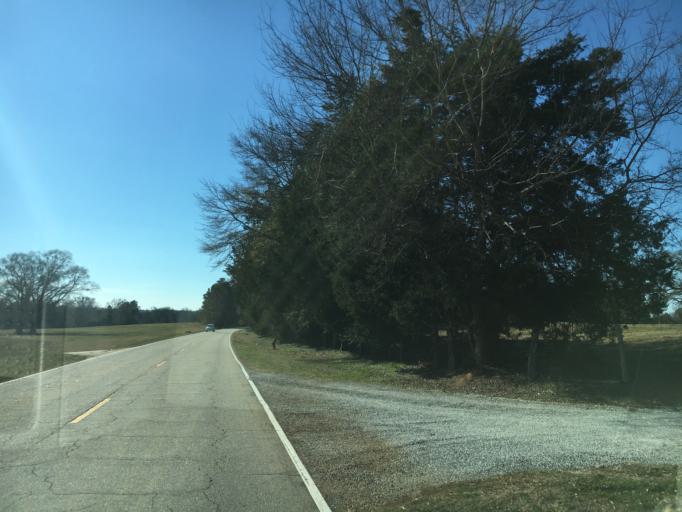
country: US
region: South Carolina
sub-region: Anderson County
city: Iva
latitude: 34.3537
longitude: -82.7290
